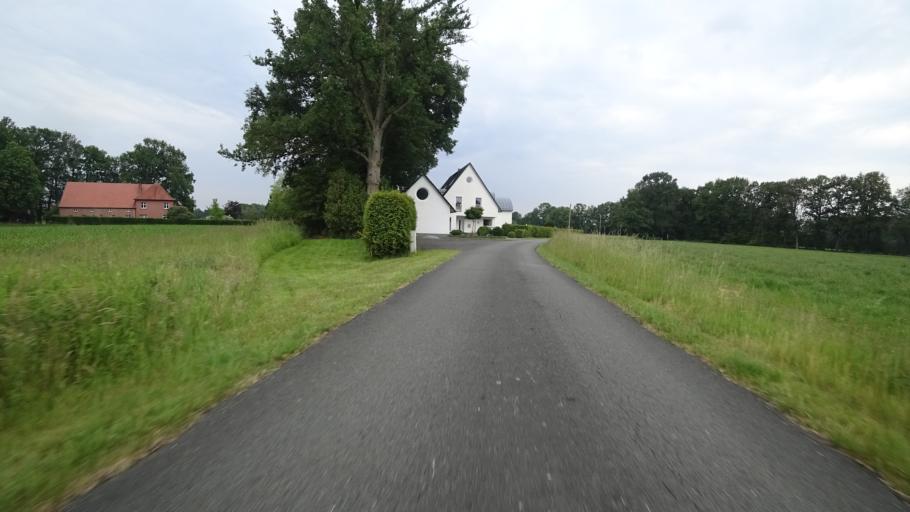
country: DE
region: North Rhine-Westphalia
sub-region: Regierungsbezirk Detmold
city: Guetersloh
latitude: 51.9534
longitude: 8.3307
